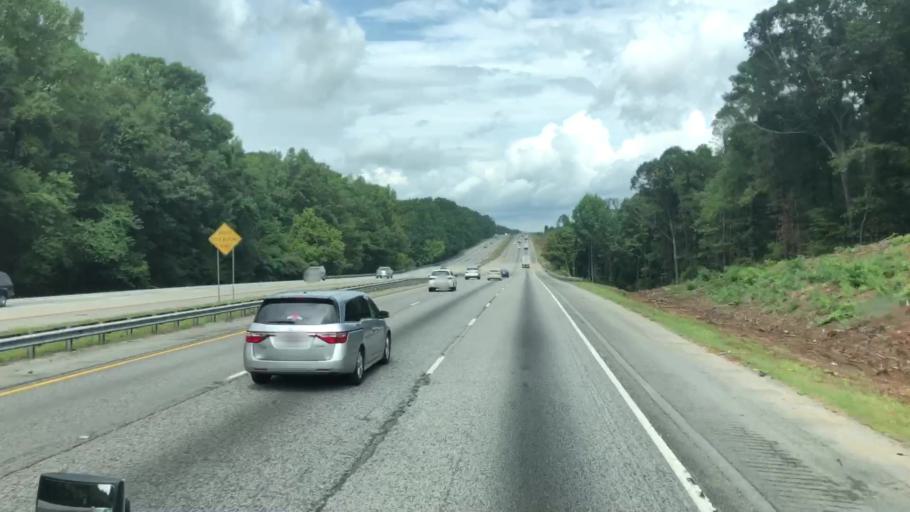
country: US
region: Georgia
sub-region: Monroe County
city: Forsyth
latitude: 33.1344
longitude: -84.0168
